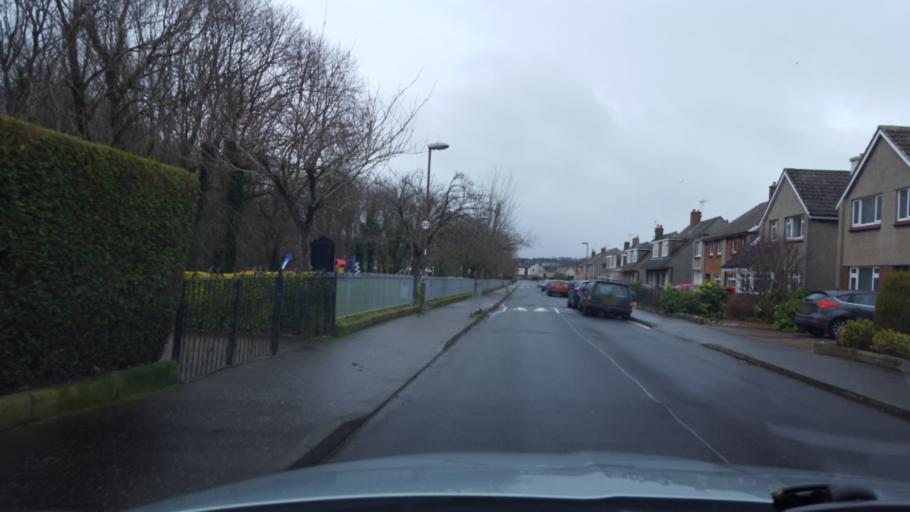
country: GB
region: Scotland
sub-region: Edinburgh
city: Currie
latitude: 55.9022
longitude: -3.3015
